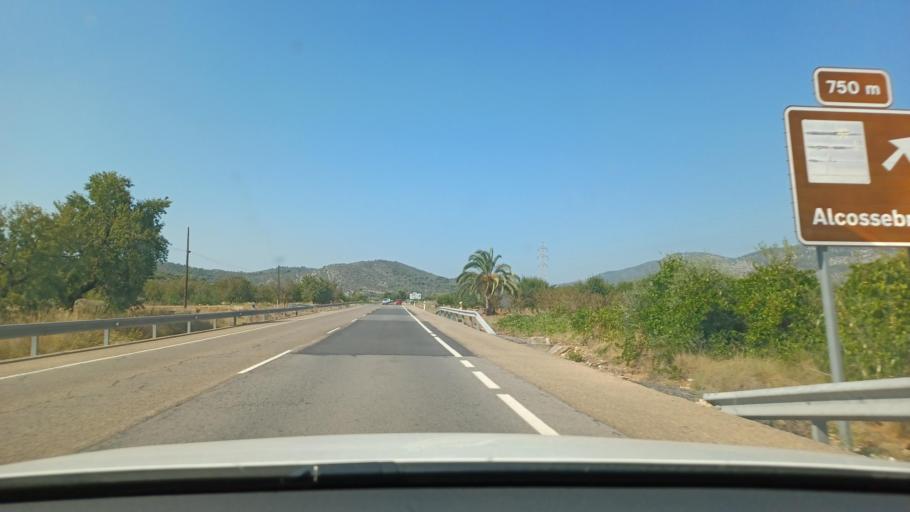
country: ES
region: Valencia
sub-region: Provincia de Castello
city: Alcala de Xivert
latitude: 40.2596
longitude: 0.2380
